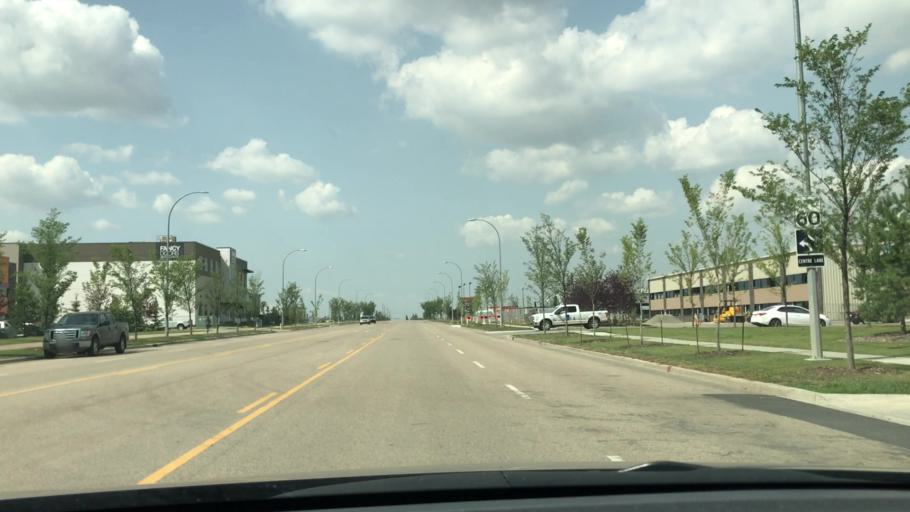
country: CA
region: Alberta
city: Edmonton
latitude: 53.4955
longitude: -113.4069
